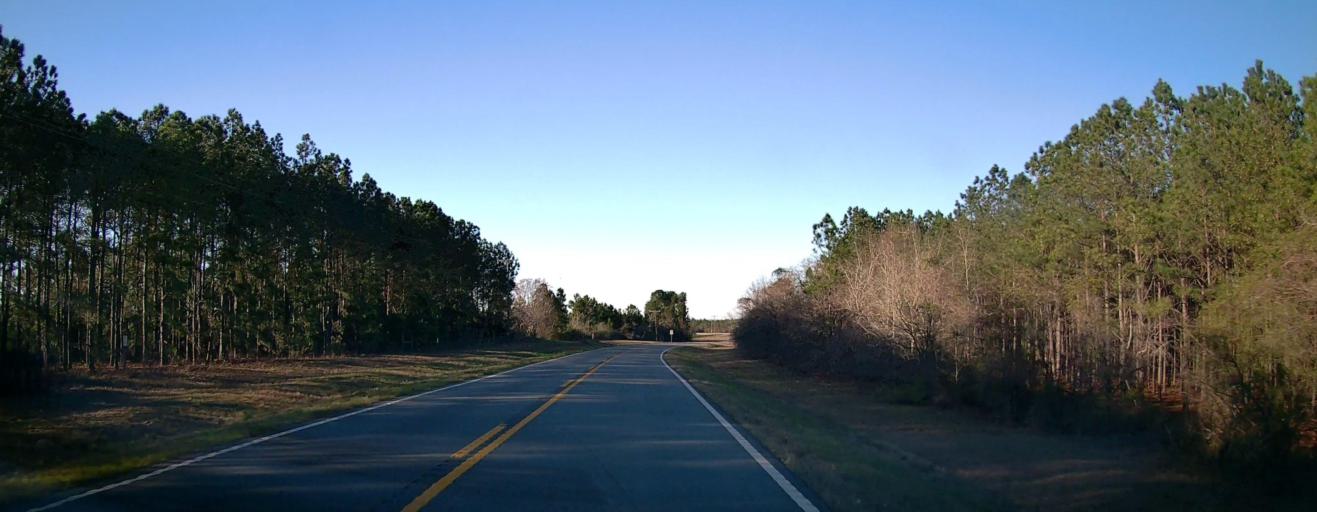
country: US
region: Georgia
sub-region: Talbot County
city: Talbotton
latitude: 32.5565
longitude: -84.4374
